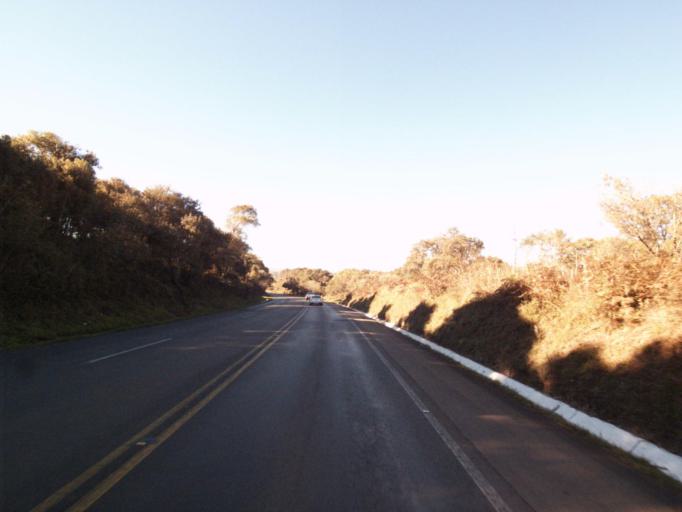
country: BR
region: Santa Catarina
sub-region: Concordia
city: Concordia
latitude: -26.8970
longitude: -51.9778
